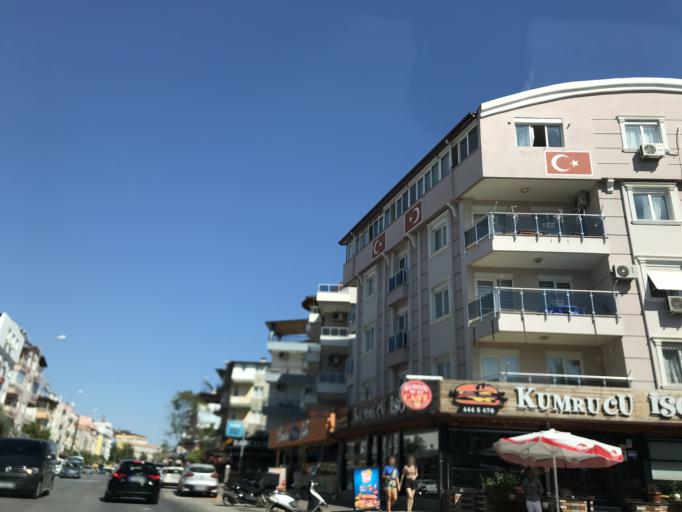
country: TR
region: Antalya
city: Antalya
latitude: 36.9029
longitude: 30.6568
